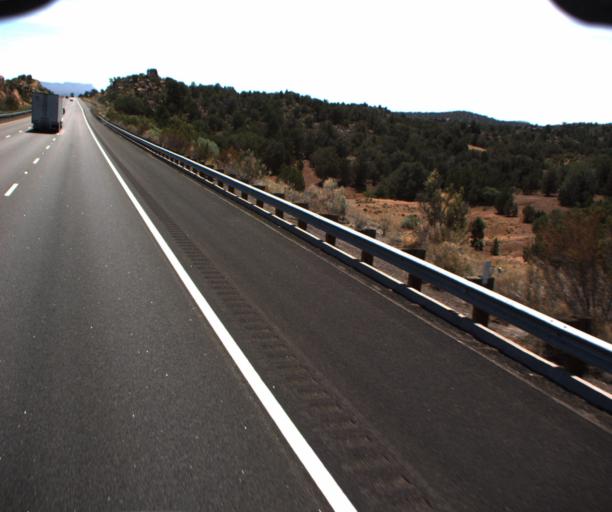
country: US
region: Arizona
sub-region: Mohave County
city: Peach Springs
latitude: 35.1847
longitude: -113.4014
